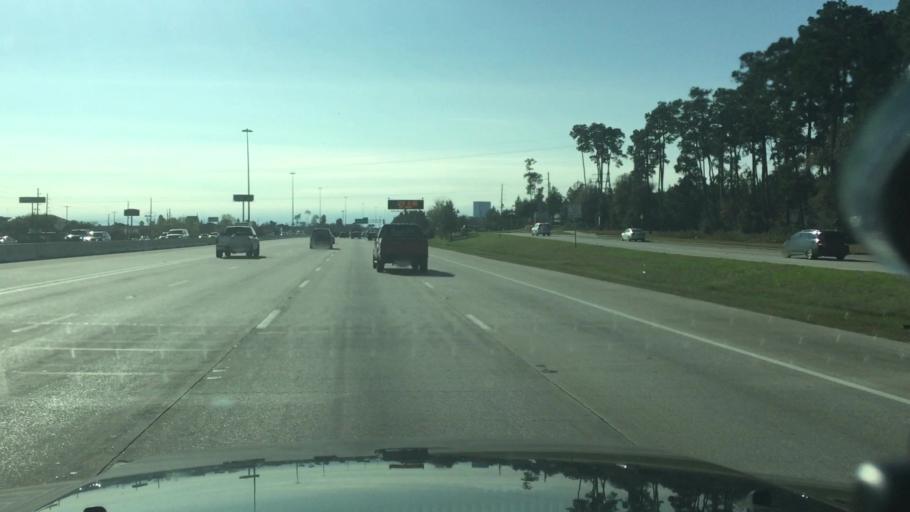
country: US
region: Texas
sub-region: Montgomery County
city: Shenandoah
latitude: 30.1949
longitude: -95.4543
